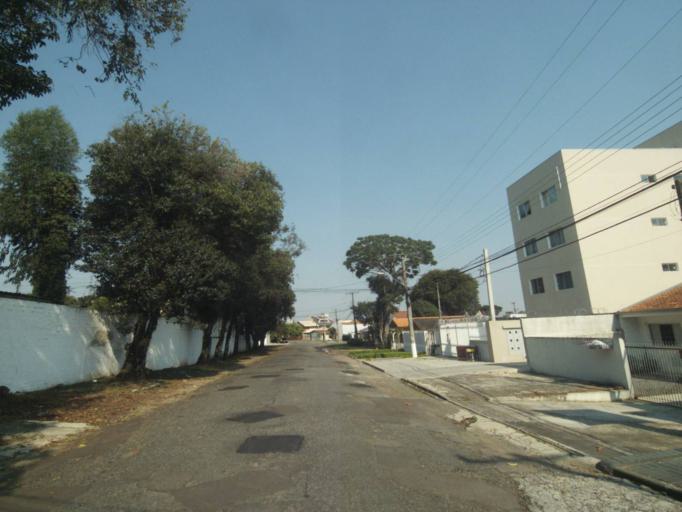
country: BR
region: Parana
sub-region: Sao Jose Dos Pinhais
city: Sao Jose dos Pinhais
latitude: -25.5029
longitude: -49.2756
